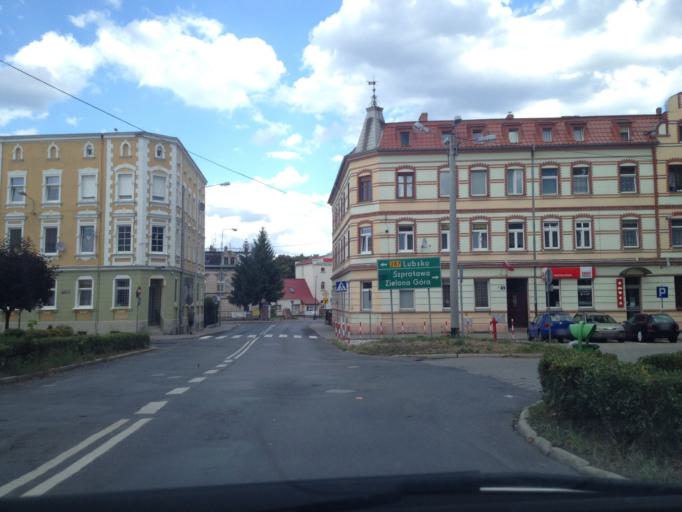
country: PL
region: Lubusz
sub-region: Powiat zarski
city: Zary
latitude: 51.6418
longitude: 15.1339
